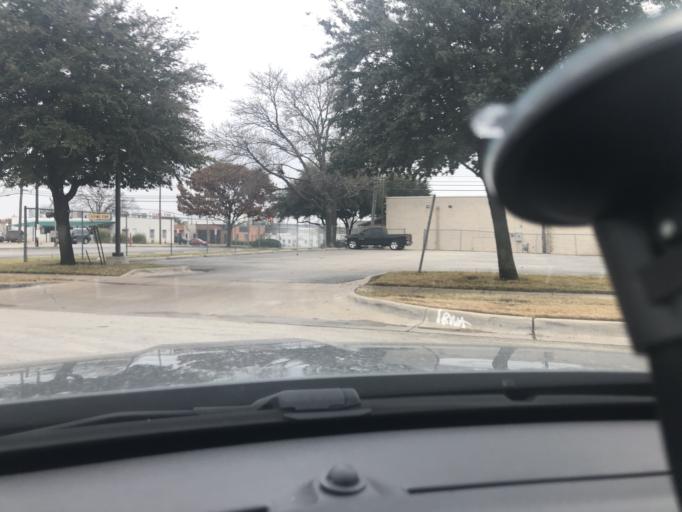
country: US
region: Texas
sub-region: Tarrant County
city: Westworth
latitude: 32.7318
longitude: -97.3706
